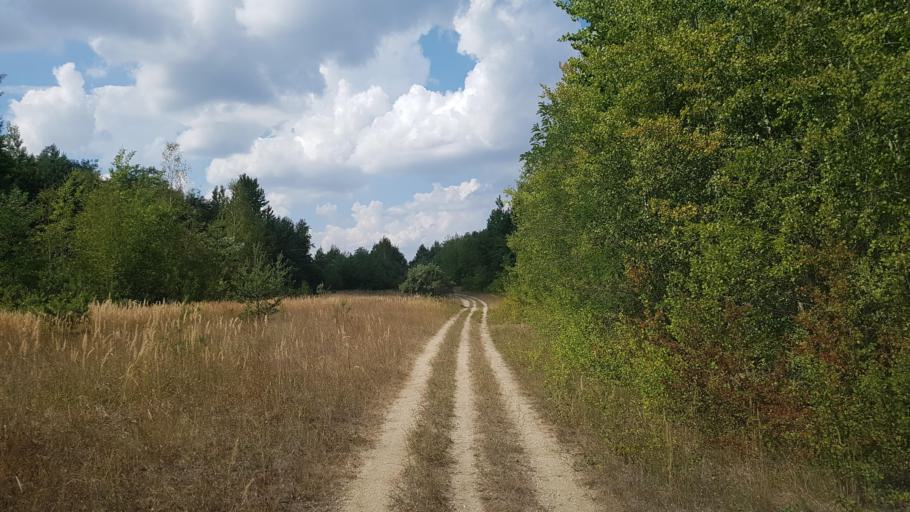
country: DE
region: Brandenburg
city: Sallgast
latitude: 51.5639
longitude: 13.8461
